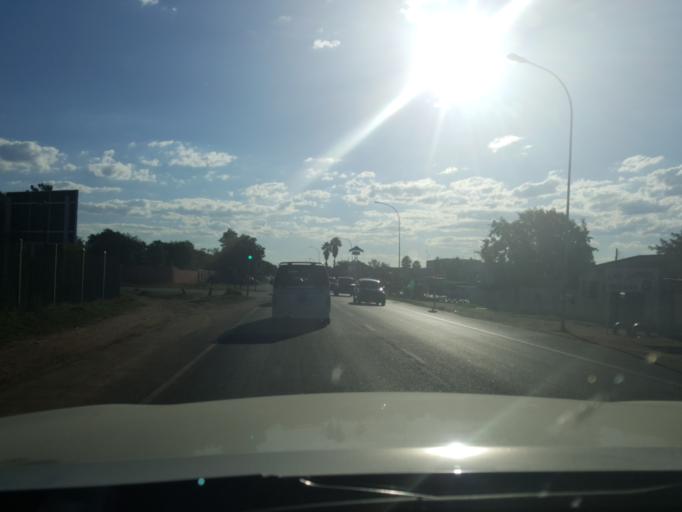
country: BW
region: South East
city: Gaborone
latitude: -24.6447
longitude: 25.9333
